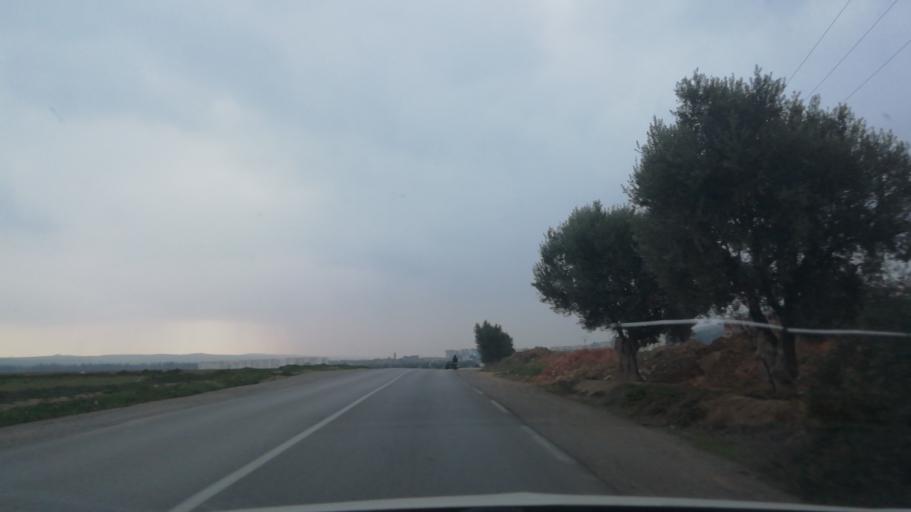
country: DZ
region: Sidi Bel Abbes
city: Sfizef
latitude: 35.2449
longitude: -0.2172
